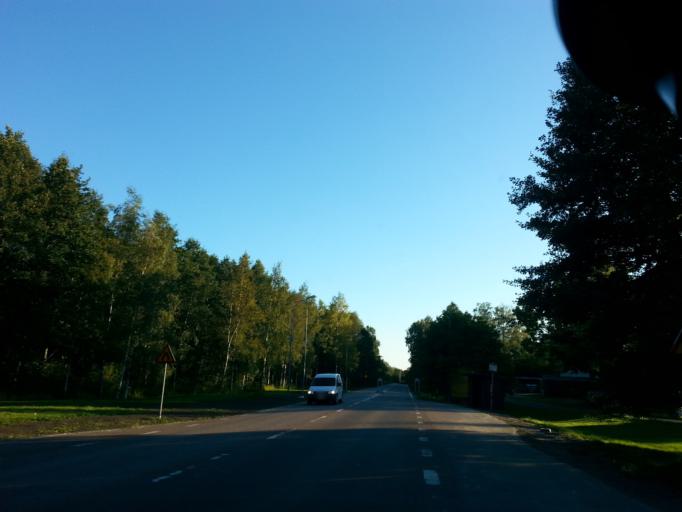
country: SE
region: Uppsala
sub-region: Osthammars Kommun
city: Oregrund
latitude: 60.3339
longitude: 18.4319
